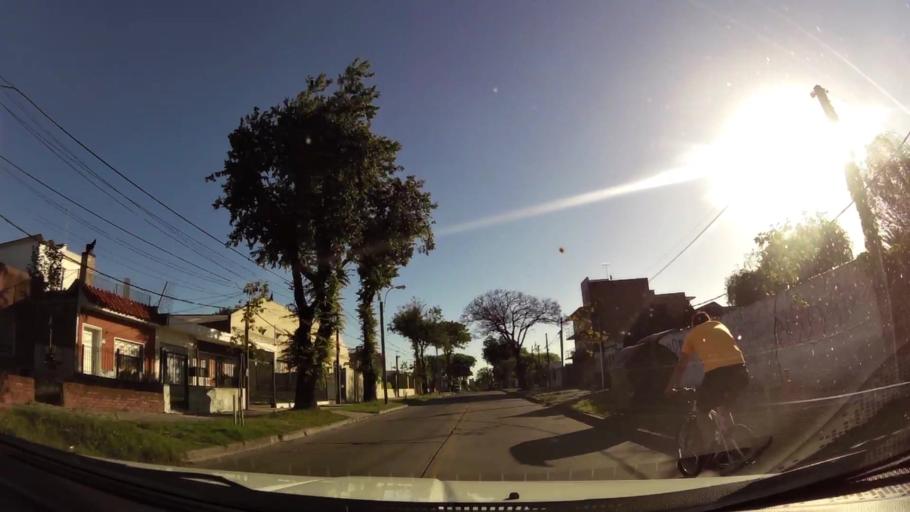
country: UY
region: Montevideo
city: Montevideo
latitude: -34.8345
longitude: -56.2117
